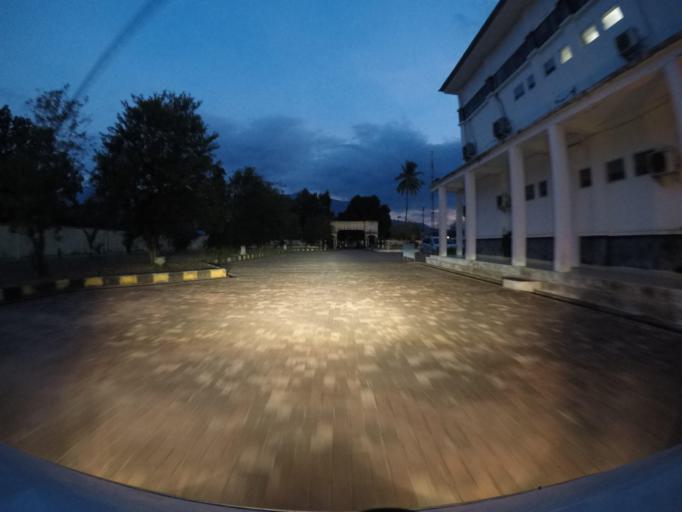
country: TL
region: Bobonaro
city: Maliana
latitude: -8.9889
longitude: 125.2084
